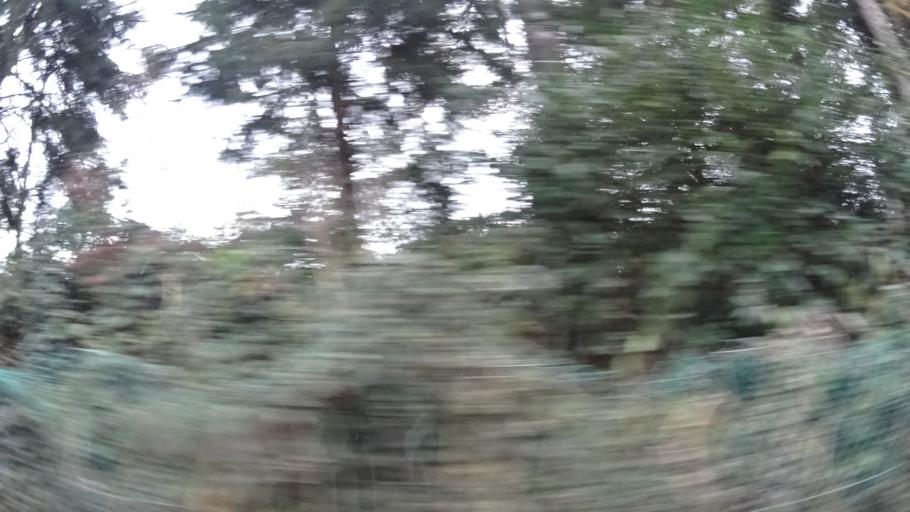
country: DE
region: Baden-Wuerttemberg
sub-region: Karlsruhe Region
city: Sinzheim
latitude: 48.7511
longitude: 8.1805
